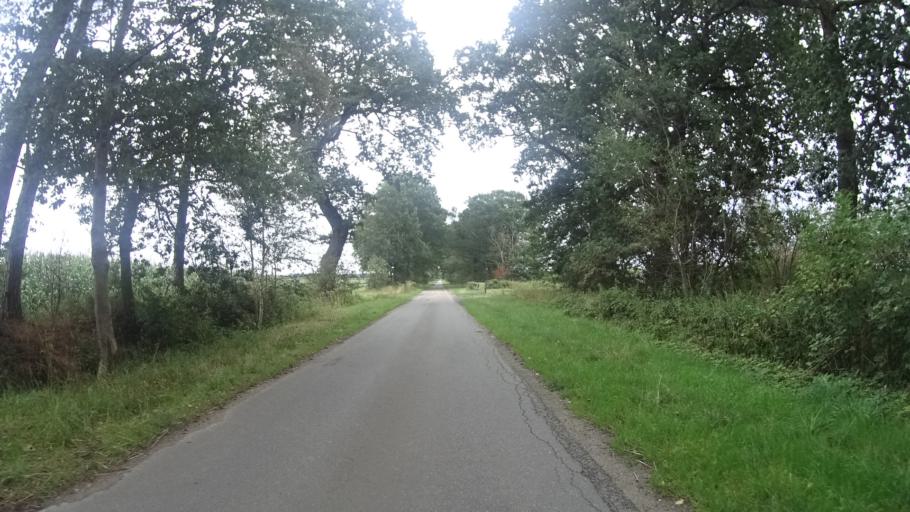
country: DE
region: Lower Saxony
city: Lintig
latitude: 53.6345
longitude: 8.9156
